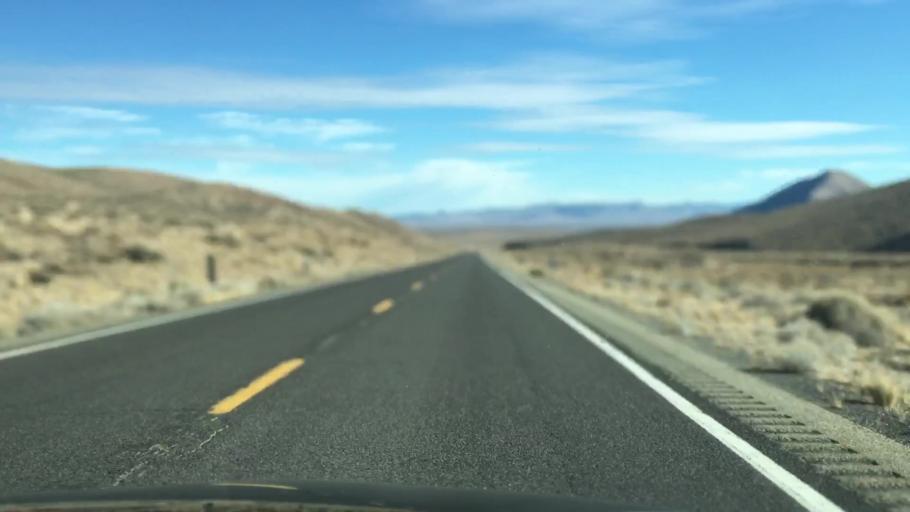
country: US
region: Nevada
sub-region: Lyon County
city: Yerington
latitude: 39.0403
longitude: -118.9387
